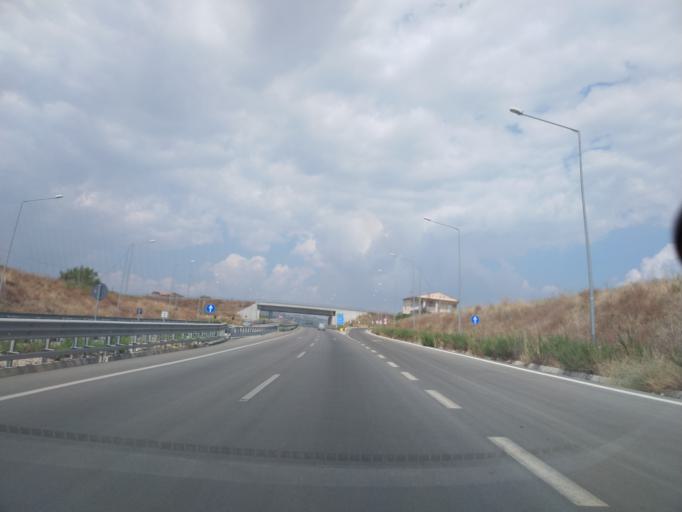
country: IT
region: Sicily
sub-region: Agrigento
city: Favara
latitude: 37.3522
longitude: 13.6792
